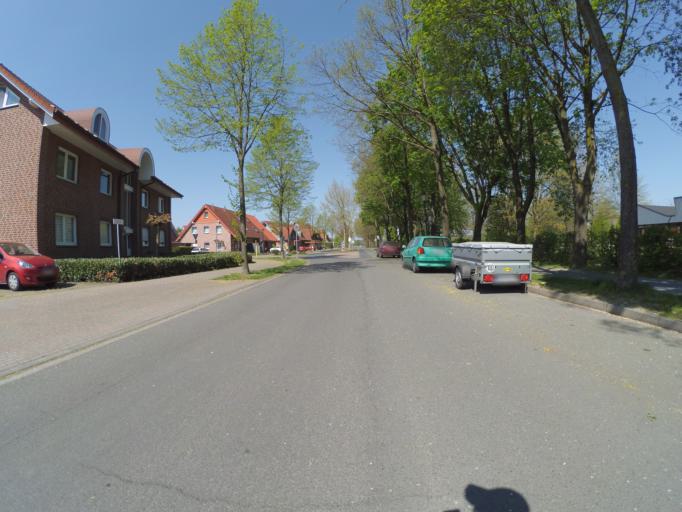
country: DE
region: North Rhine-Westphalia
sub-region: Regierungsbezirk Munster
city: Nordkirchen
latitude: 51.7433
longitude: 7.5268
